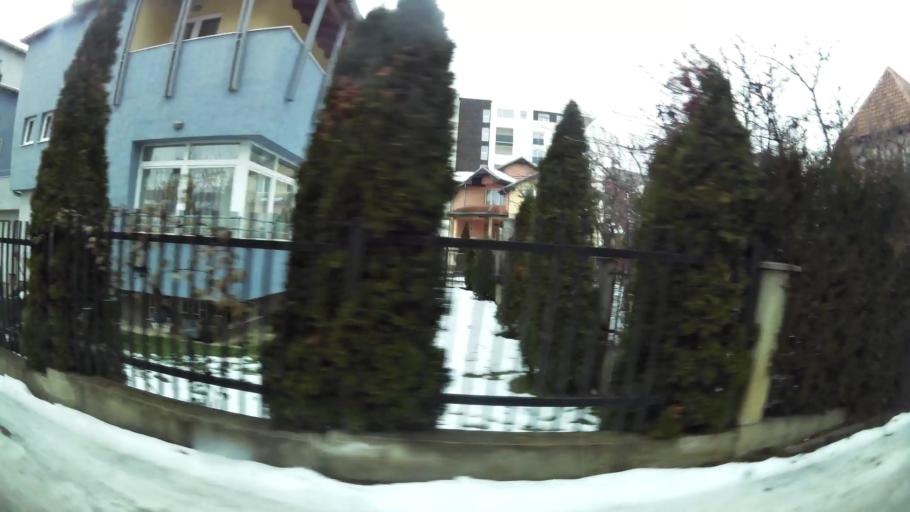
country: XK
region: Pristina
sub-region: Komuna e Prishtines
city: Pristina
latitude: 42.6447
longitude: 21.1800
